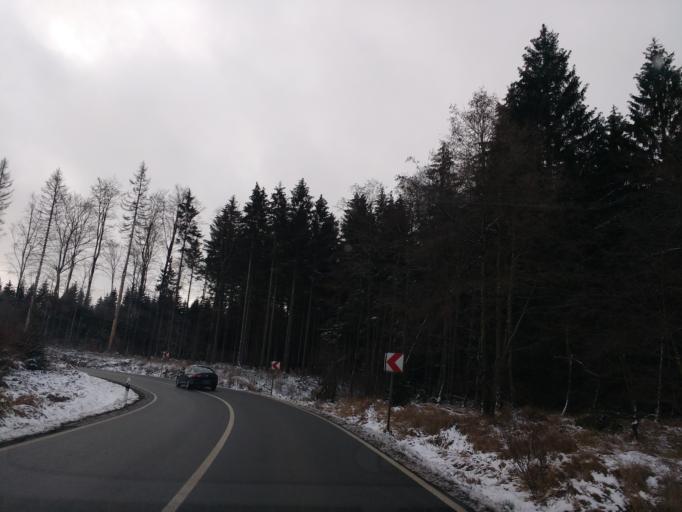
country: DE
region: Saxony-Anhalt
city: Friedrichsbrunn
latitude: 51.6988
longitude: 11.0507
